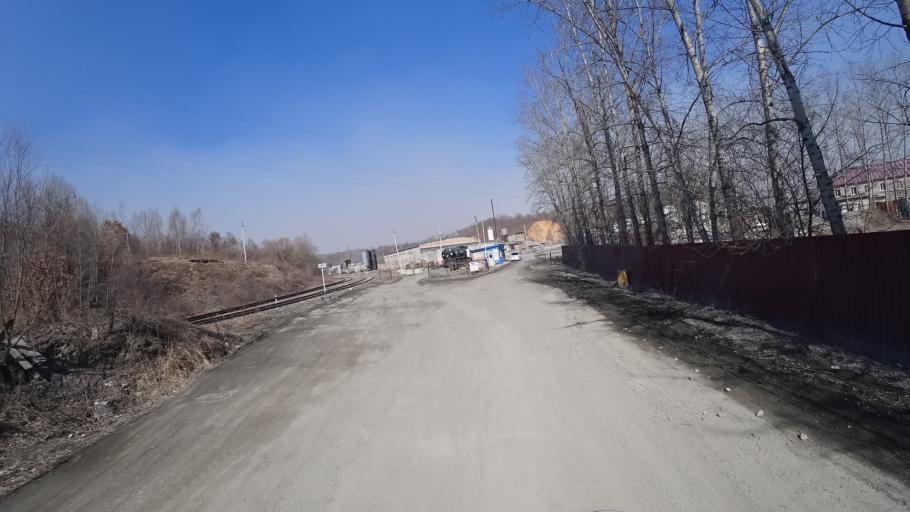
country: RU
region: Amur
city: Novobureyskiy
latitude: 49.7894
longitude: 129.9596
